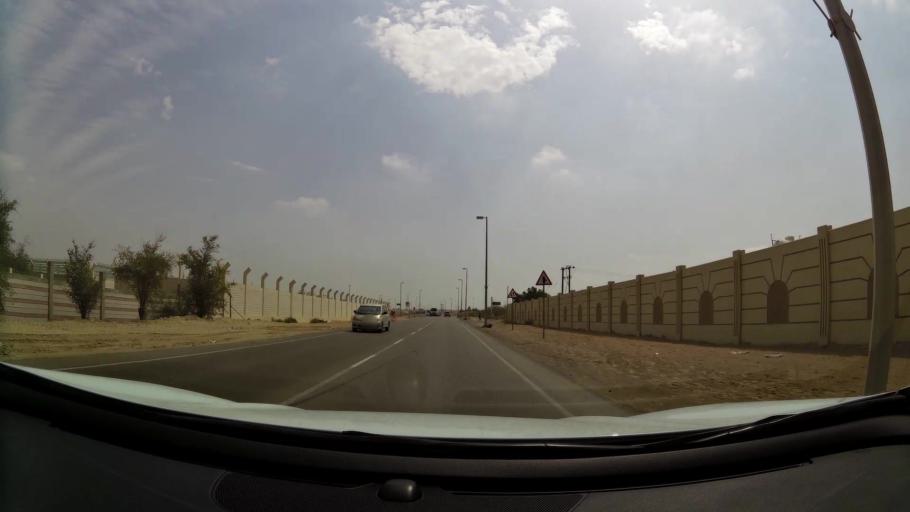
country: AE
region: Abu Dhabi
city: Abu Dhabi
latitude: 24.5158
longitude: 54.6576
